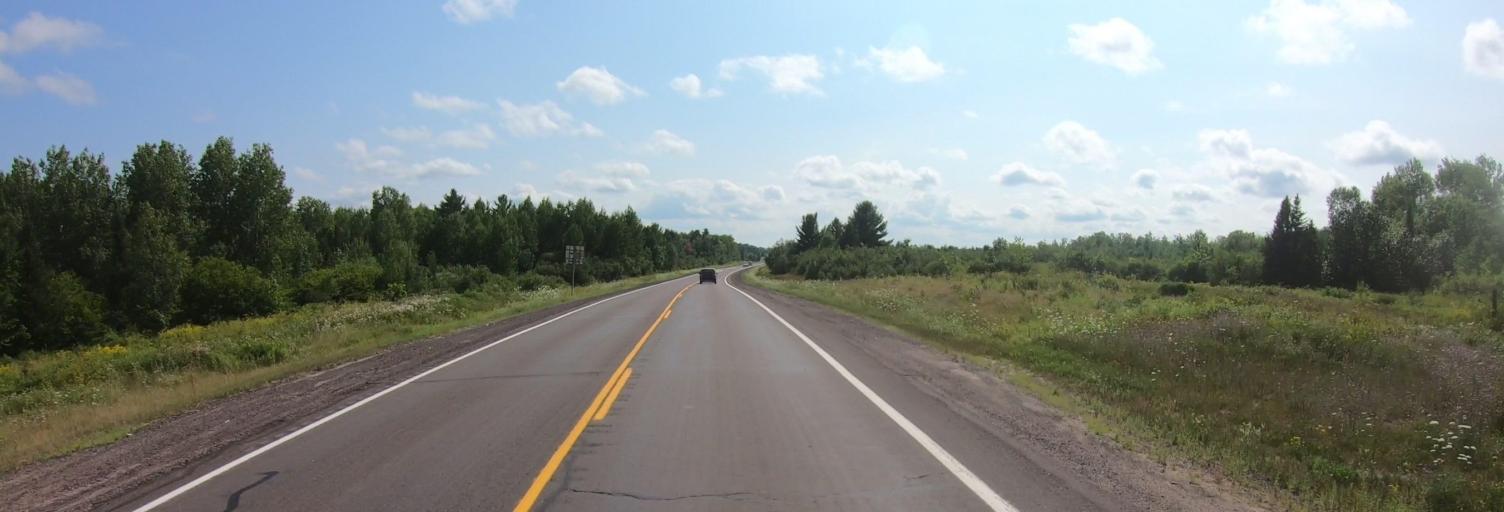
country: US
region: Michigan
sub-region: Ontonagon County
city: Ontonagon
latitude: 46.7282
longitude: -89.1491
